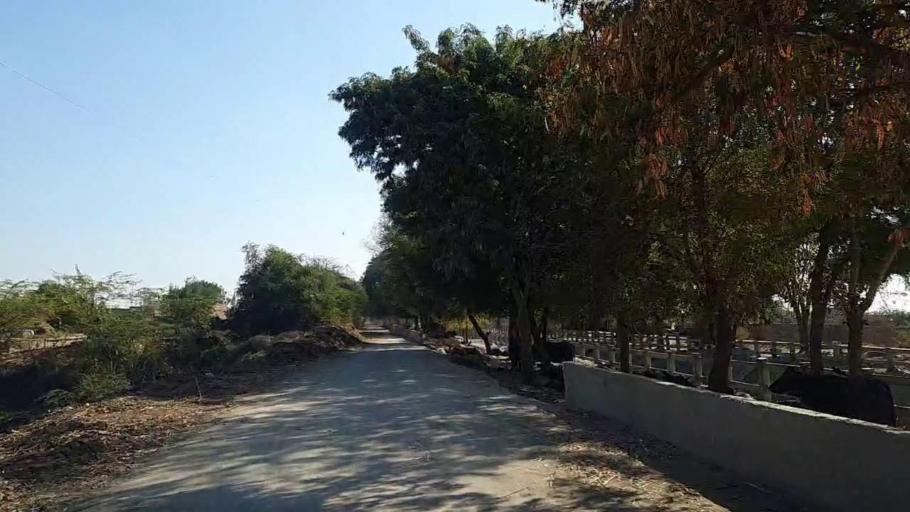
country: PK
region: Sindh
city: Nawabshah
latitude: 26.2605
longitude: 68.4170
